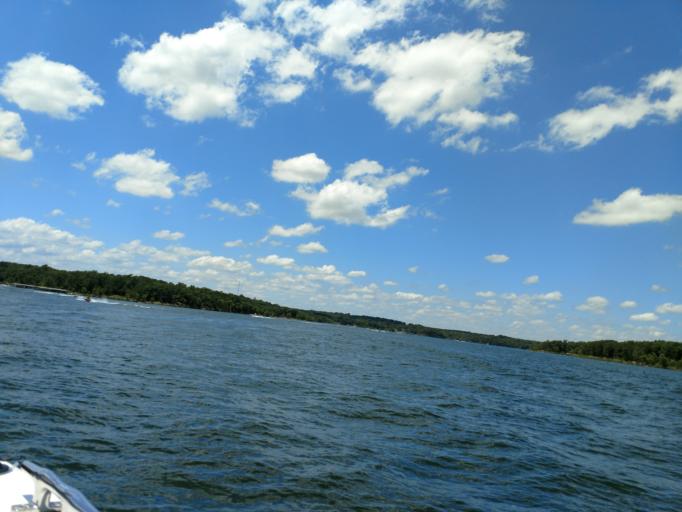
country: US
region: Missouri
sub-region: Barry County
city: Shell Knob
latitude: 36.5885
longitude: -93.5623
